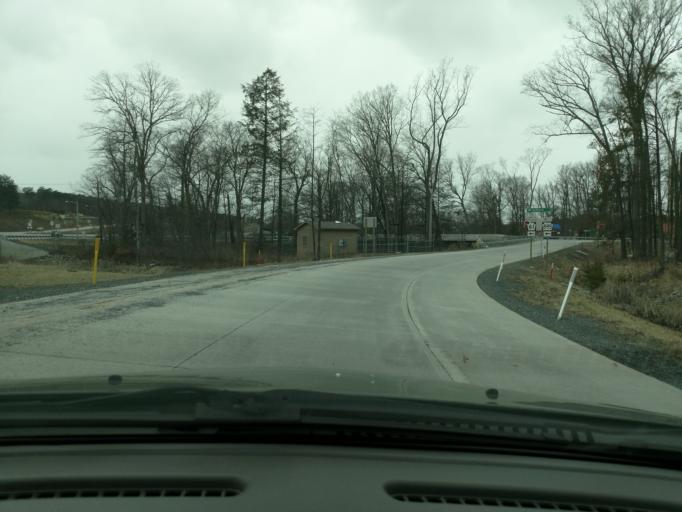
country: US
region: Pennsylvania
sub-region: Schuylkill County
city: Orwigsburg
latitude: 40.6190
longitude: -76.0568
